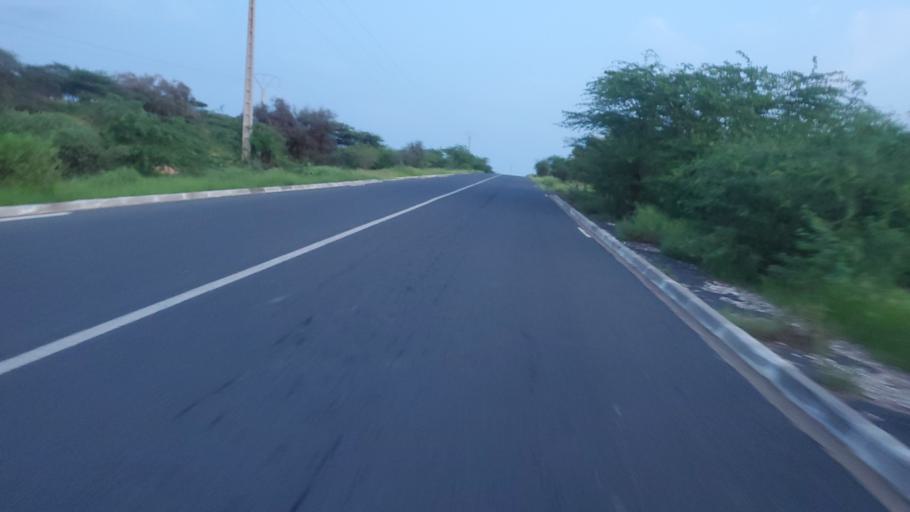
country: SN
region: Saint-Louis
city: Saint-Louis
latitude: 16.0775
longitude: -16.3903
